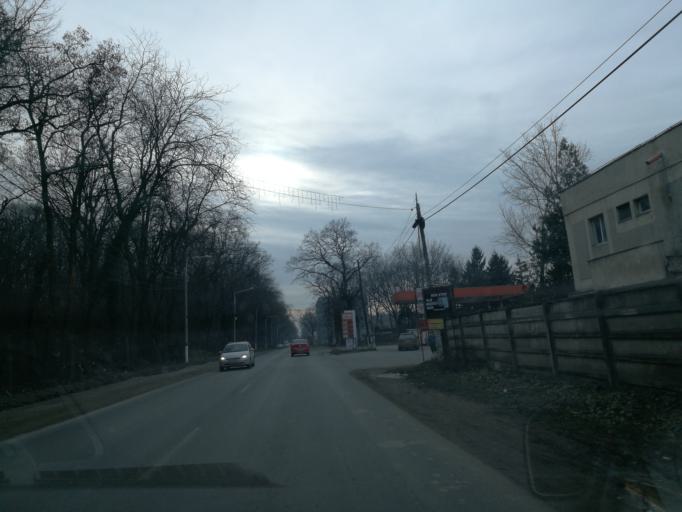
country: RO
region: Ilfov
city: Stefanestii de Jos
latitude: 44.5218
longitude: 26.1949
